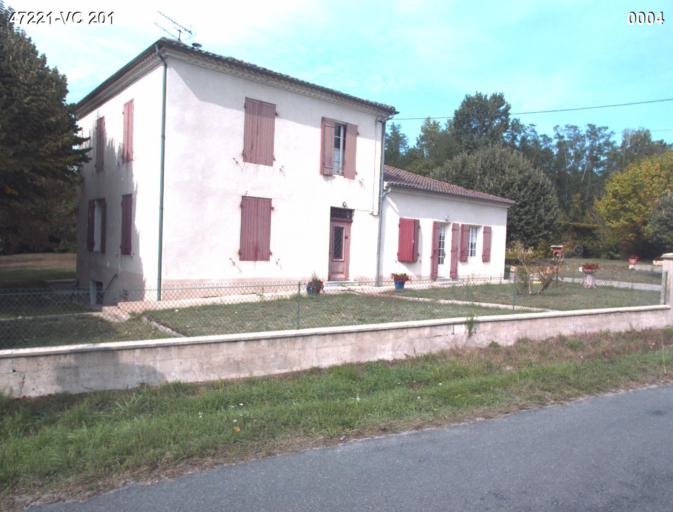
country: FR
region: Aquitaine
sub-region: Departement du Lot-et-Garonne
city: Mezin
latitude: 44.1193
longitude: 0.2238
